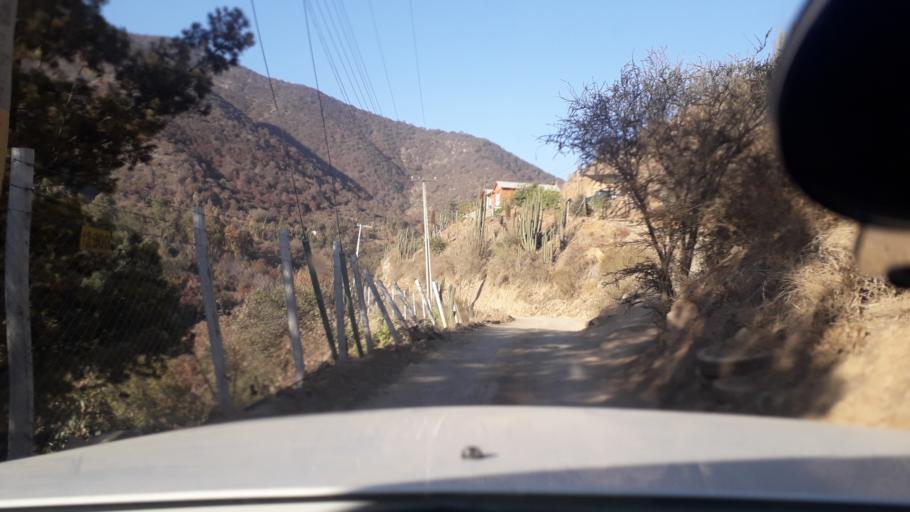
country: CL
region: Valparaiso
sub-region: Provincia de Marga Marga
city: Limache
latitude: -33.0520
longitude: -71.0874
